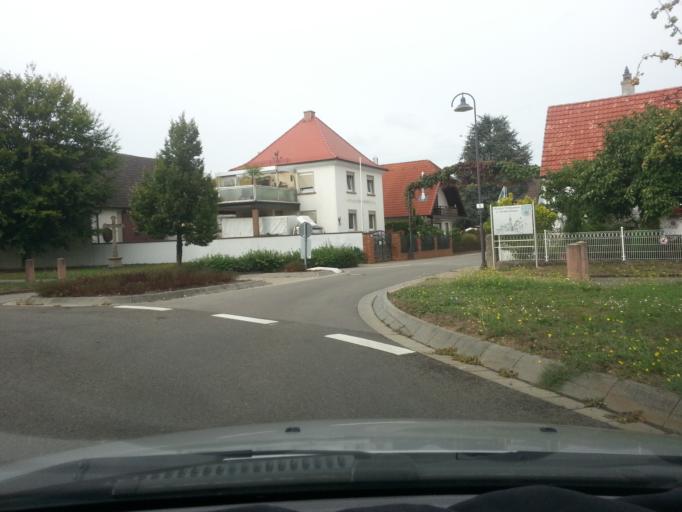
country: DE
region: Rheinland-Pfalz
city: Grossfischlingen
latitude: 49.2670
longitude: 8.1751
